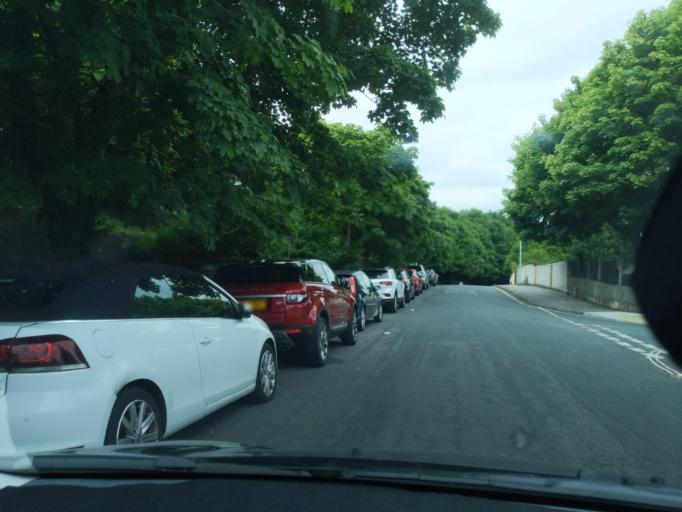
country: GB
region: England
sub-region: Plymouth
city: Plymouth
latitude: 50.4072
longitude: -4.1261
